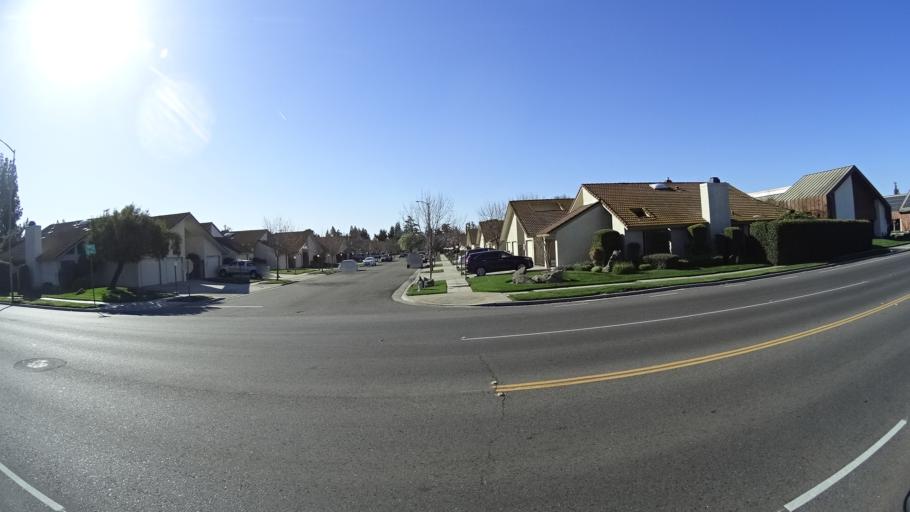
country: US
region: California
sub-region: Fresno County
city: Fresno
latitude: 36.8228
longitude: -119.8426
